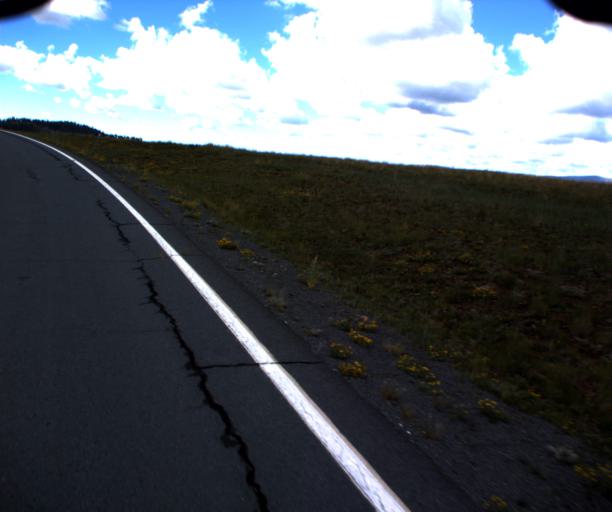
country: US
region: Arizona
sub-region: Apache County
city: Eagar
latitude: 33.9445
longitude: -109.4059
